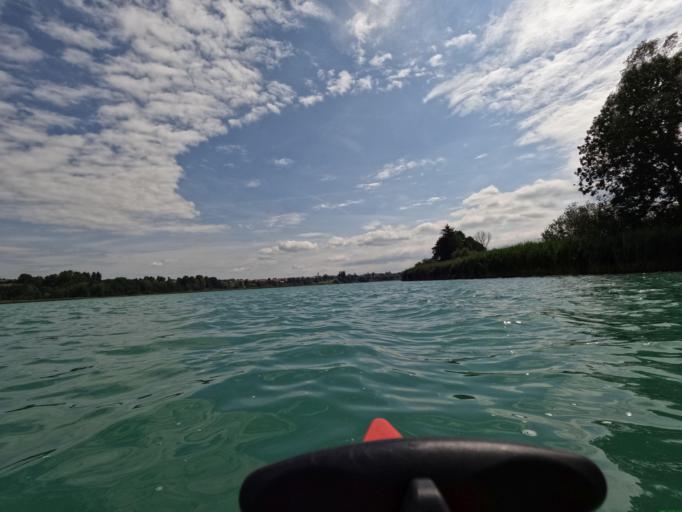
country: DE
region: Bavaria
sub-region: Upper Bavaria
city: Taching am See
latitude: 47.9582
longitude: 12.7383
